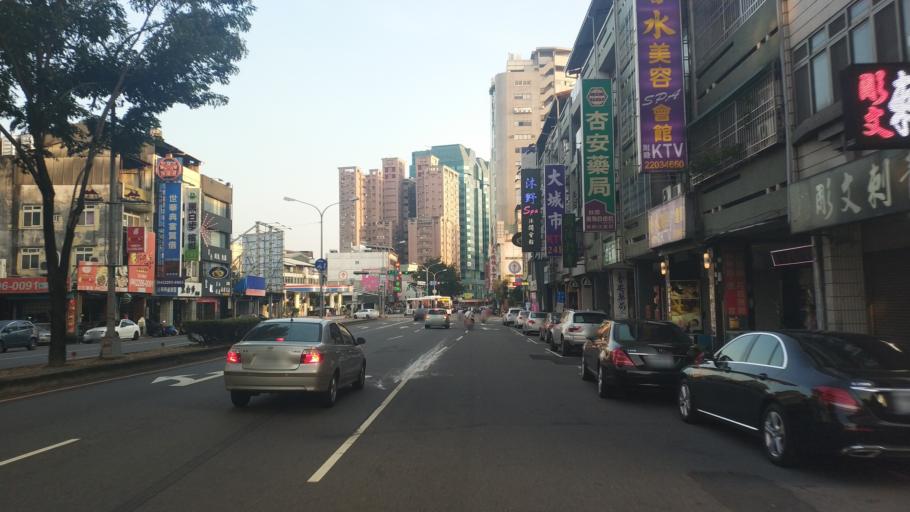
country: TW
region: Taiwan
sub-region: Taichung City
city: Taichung
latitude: 24.1567
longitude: 120.6765
